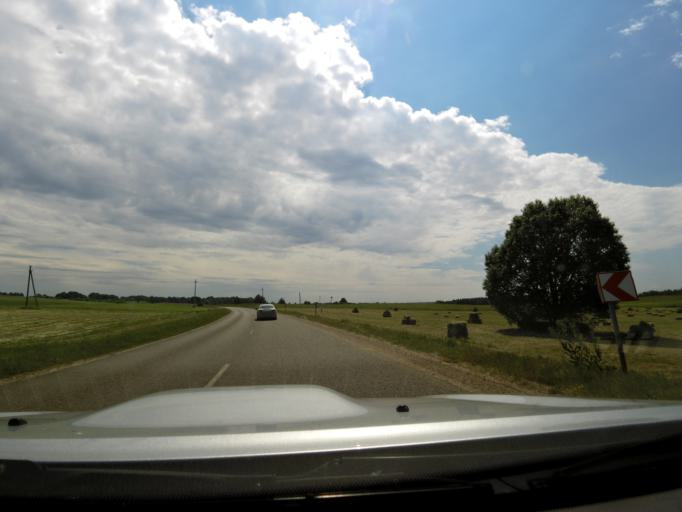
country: LT
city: Vilkaviskis
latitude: 54.5211
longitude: 23.0235
